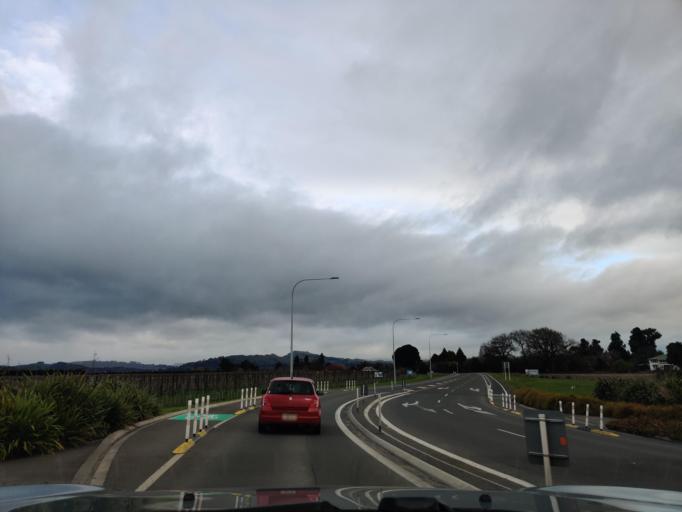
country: NZ
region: Hawke's Bay
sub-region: Hastings District
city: Hastings
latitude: -39.6200
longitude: 176.8938
